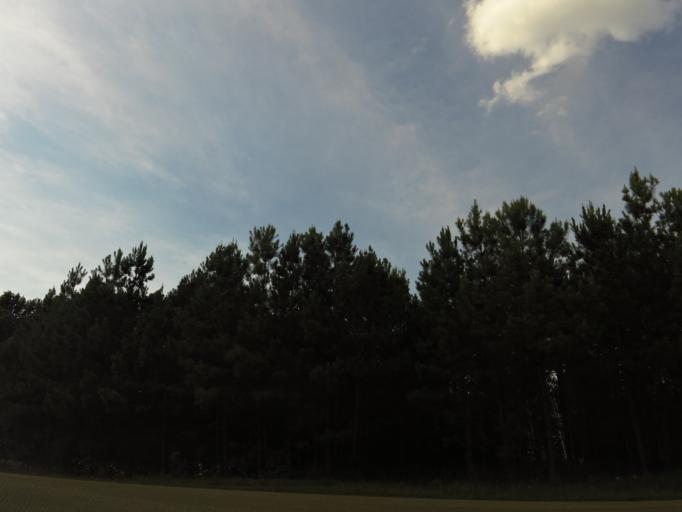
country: US
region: Tennessee
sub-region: Benton County
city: Camden
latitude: 36.0571
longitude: -88.1667
